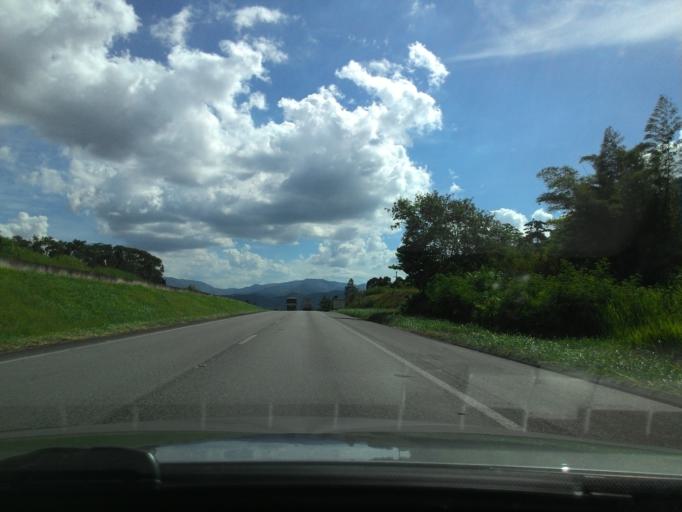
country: BR
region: Sao Paulo
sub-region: Cajati
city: Cajati
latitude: -24.7446
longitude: -48.1449
